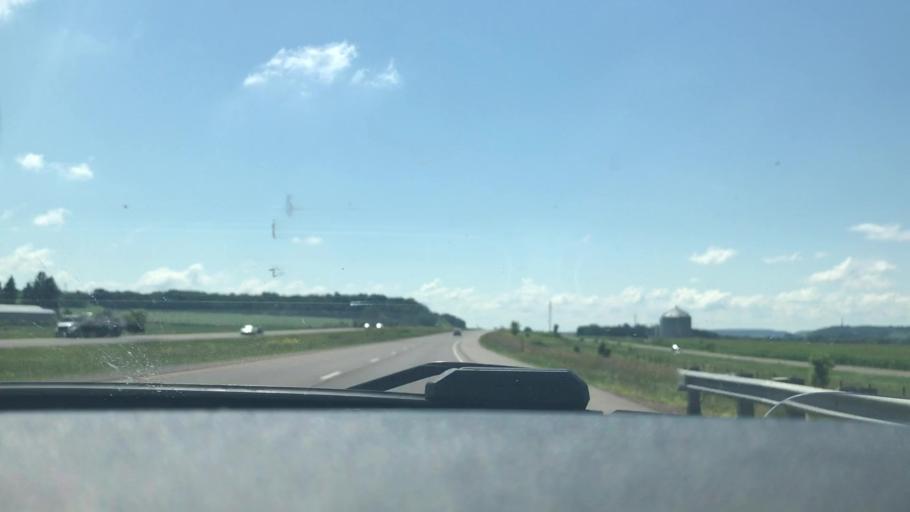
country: US
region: Wisconsin
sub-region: Chippewa County
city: Bloomer
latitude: 45.0356
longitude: -91.4545
